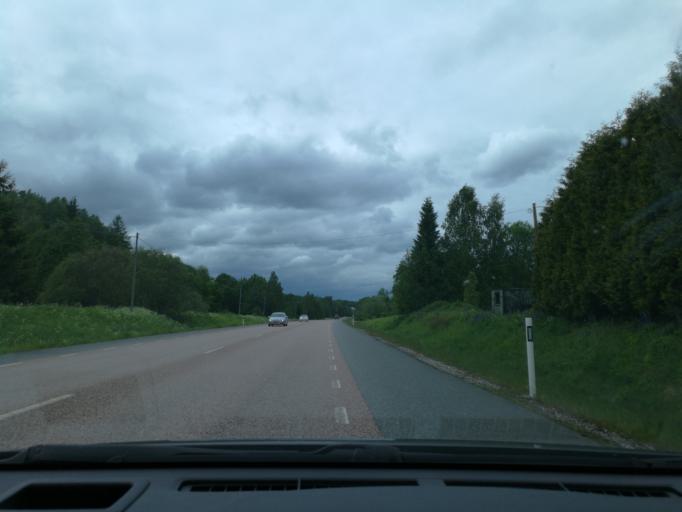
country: SE
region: Vaestmanland
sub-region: Fagersta Kommun
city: Fagersta
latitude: 59.9825
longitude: 15.6872
